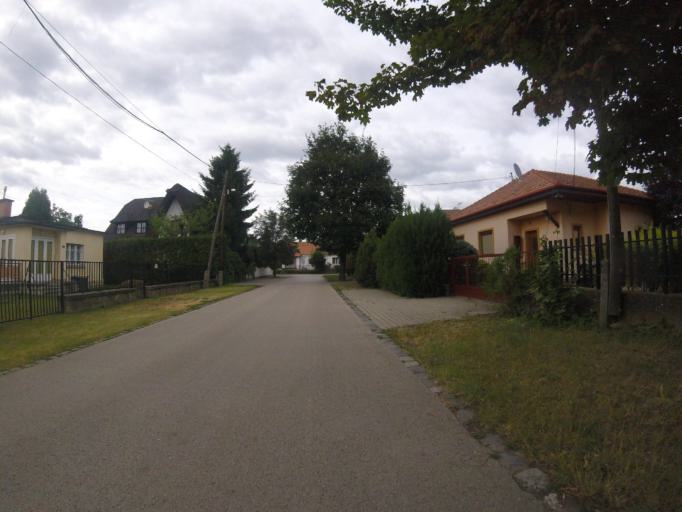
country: HU
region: Pest
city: Budakalasz
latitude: 47.5911
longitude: 19.0603
